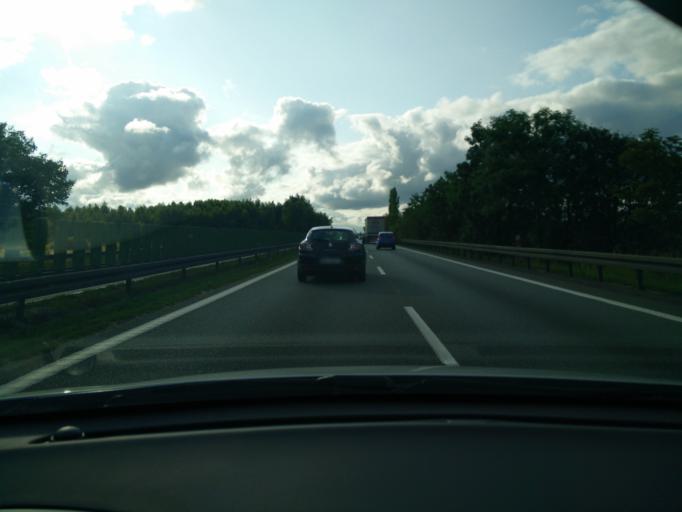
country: PL
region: Pomeranian Voivodeship
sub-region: Powiat gdanski
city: Kowale
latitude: 54.2991
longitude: 18.5777
